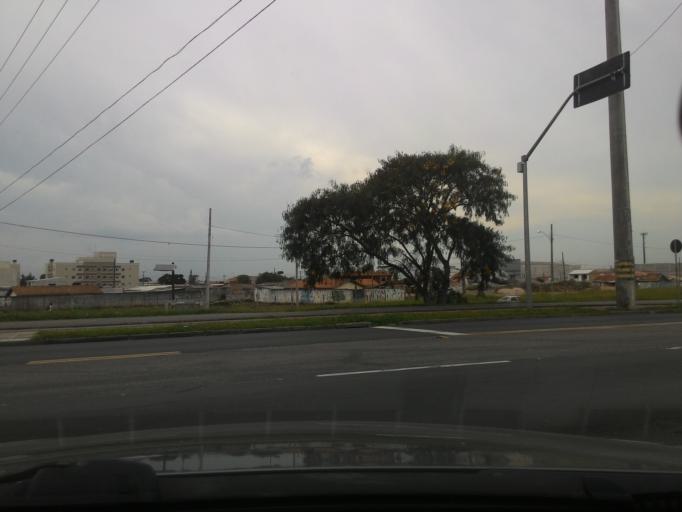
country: BR
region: Parana
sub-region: Pinhais
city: Pinhais
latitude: -25.4423
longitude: -49.1837
